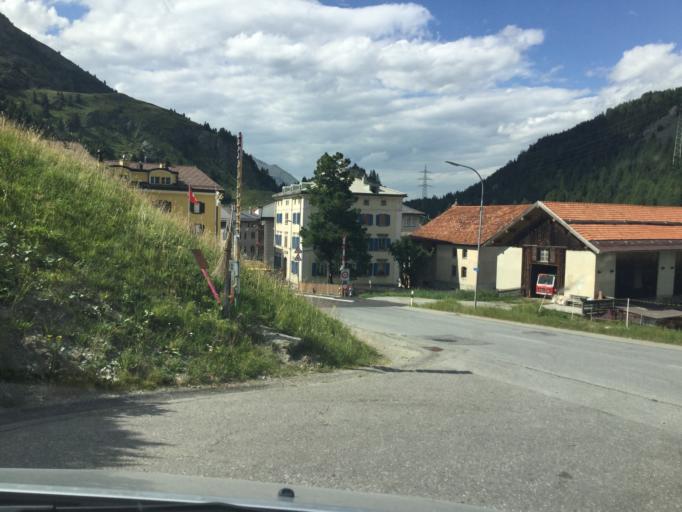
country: CH
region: Grisons
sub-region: Maloja District
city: Silvaplana
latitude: 46.4669
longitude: 9.6512
